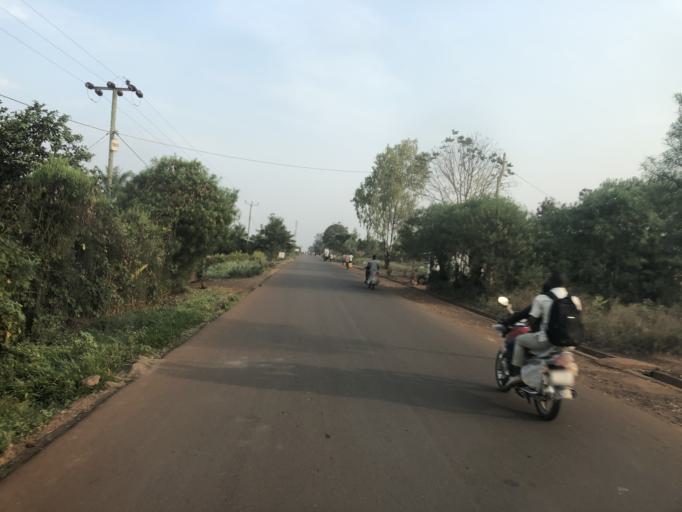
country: BI
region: Cibitoke
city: Cibitoke
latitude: -2.7239
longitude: 29.0043
